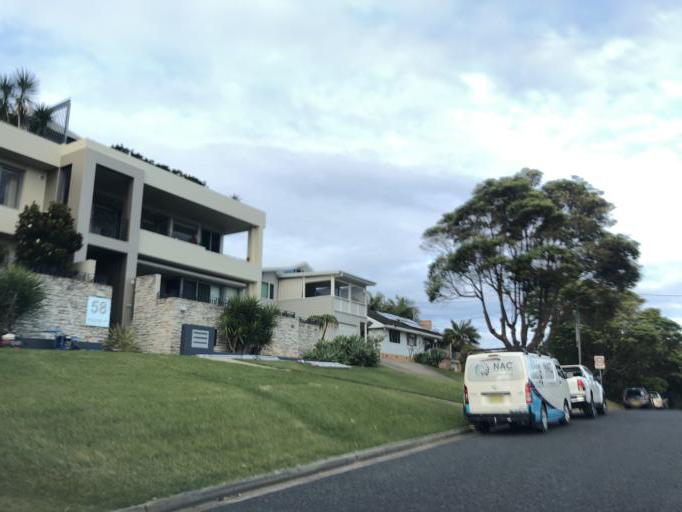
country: AU
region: New South Wales
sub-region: Coffs Harbour
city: Coffs Harbour
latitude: -30.3023
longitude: 153.1346
